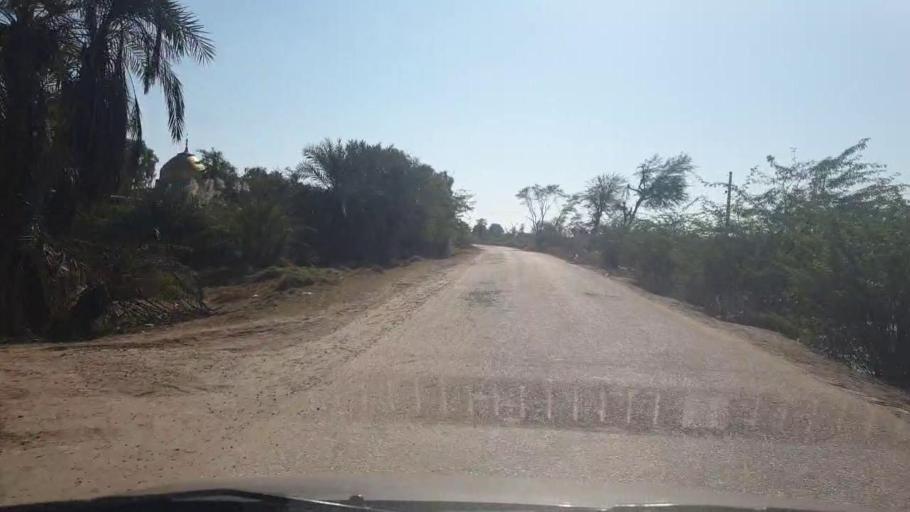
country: PK
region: Sindh
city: Bozdar
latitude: 27.1220
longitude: 68.6322
